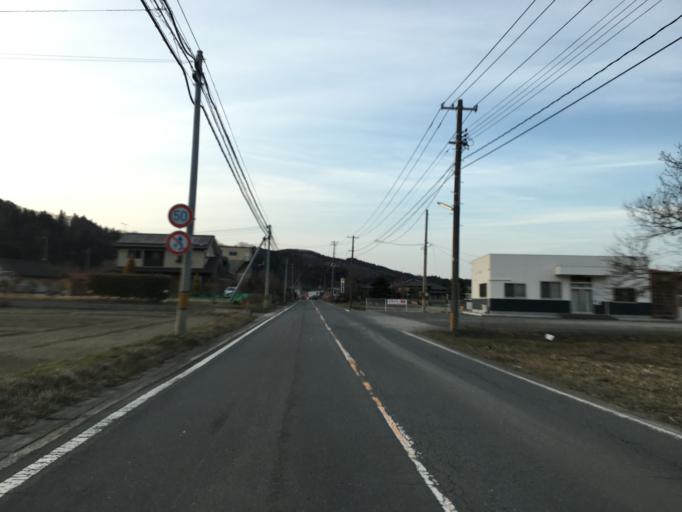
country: JP
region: Ibaraki
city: Daigo
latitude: 36.9346
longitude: 140.4080
